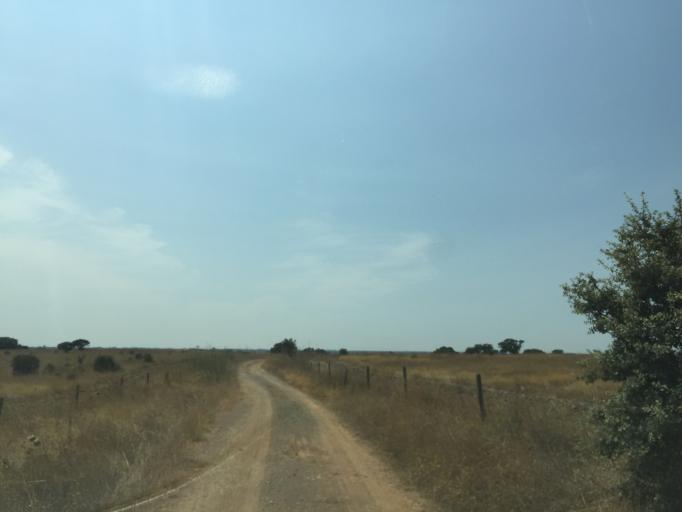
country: PT
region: Setubal
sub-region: Grandola
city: Grandola
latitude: 38.0560
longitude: -8.4417
